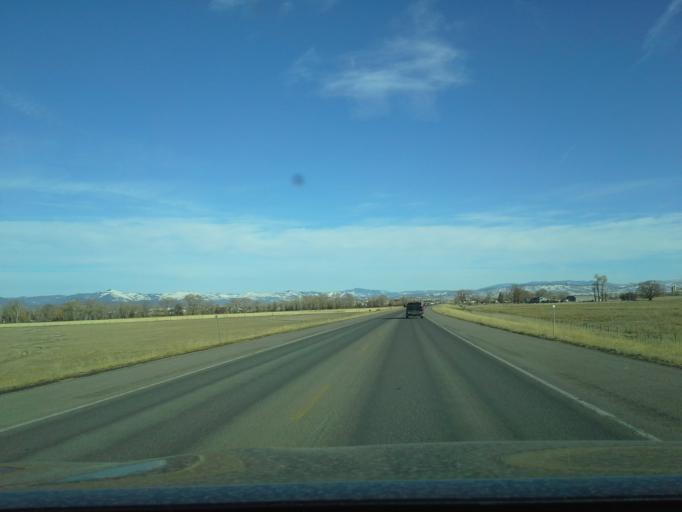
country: US
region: Montana
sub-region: Lewis and Clark County
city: Helena Valley Southeast
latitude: 46.6167
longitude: -111.9726
